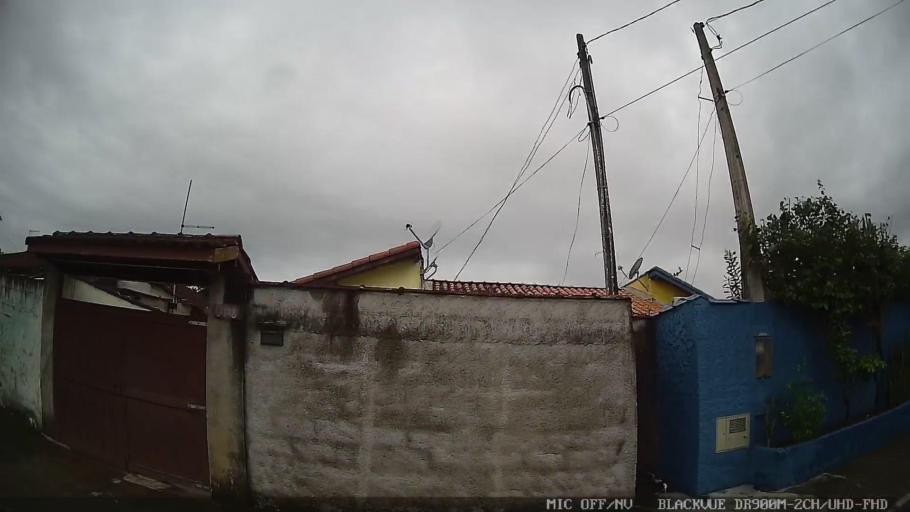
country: BR
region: Sao Paulo
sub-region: Sao Sebastiao
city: Sao Sebastiao
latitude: -23.7242
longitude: -45.4385
